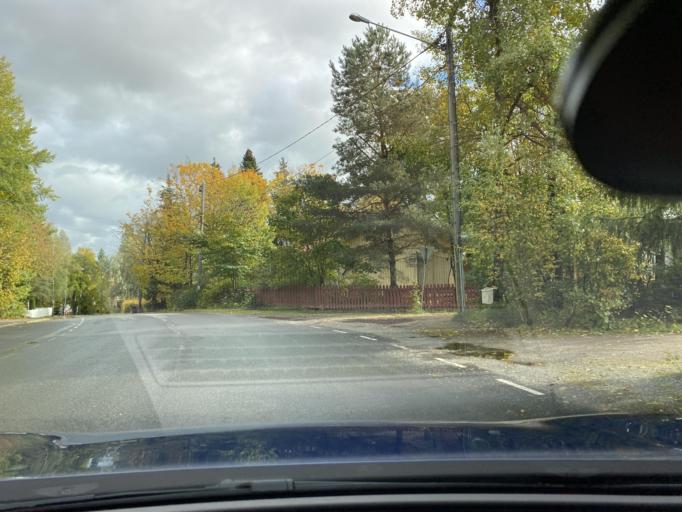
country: FI
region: Pirkanmaa
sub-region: Tampere
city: Nokia
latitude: 61.4767
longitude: 23.3408
